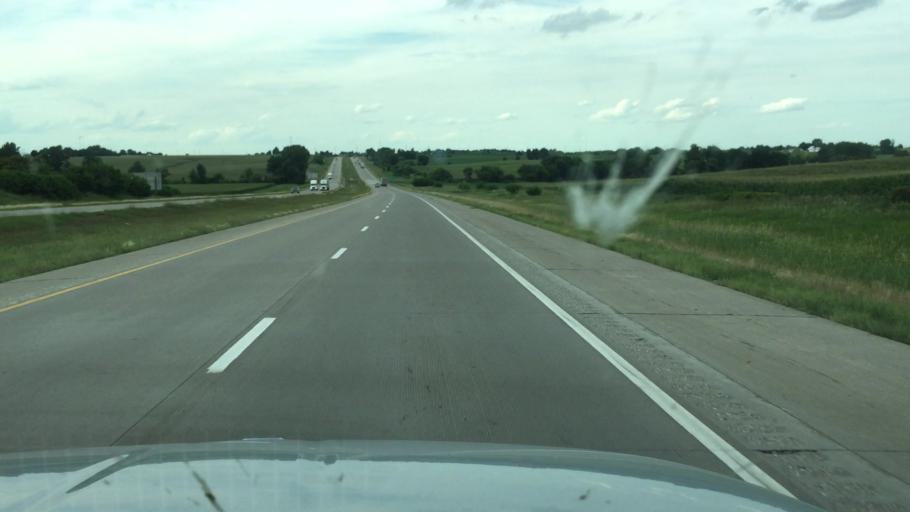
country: US
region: Iowa
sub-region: Scott County
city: Blue Grass
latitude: 41.5504
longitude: -90.6779
